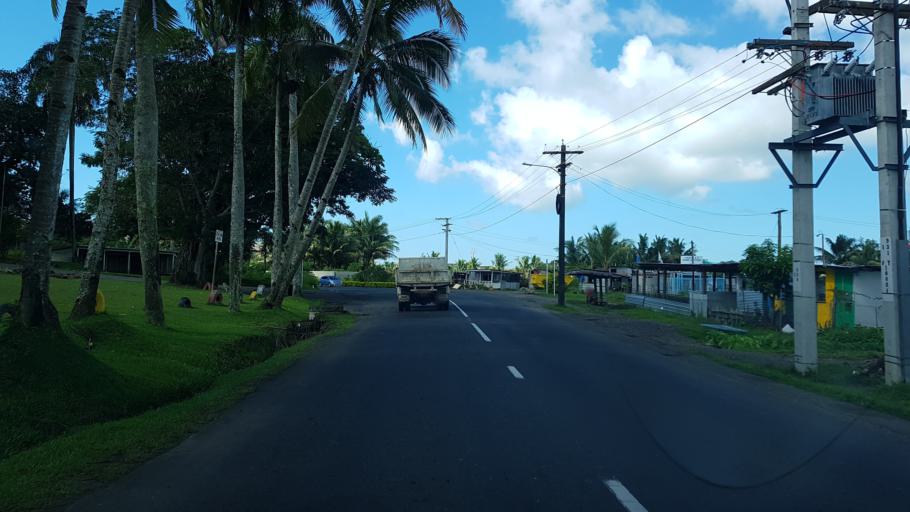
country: FJ
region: Central
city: Suva
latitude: -18.1438
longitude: 178.4542
